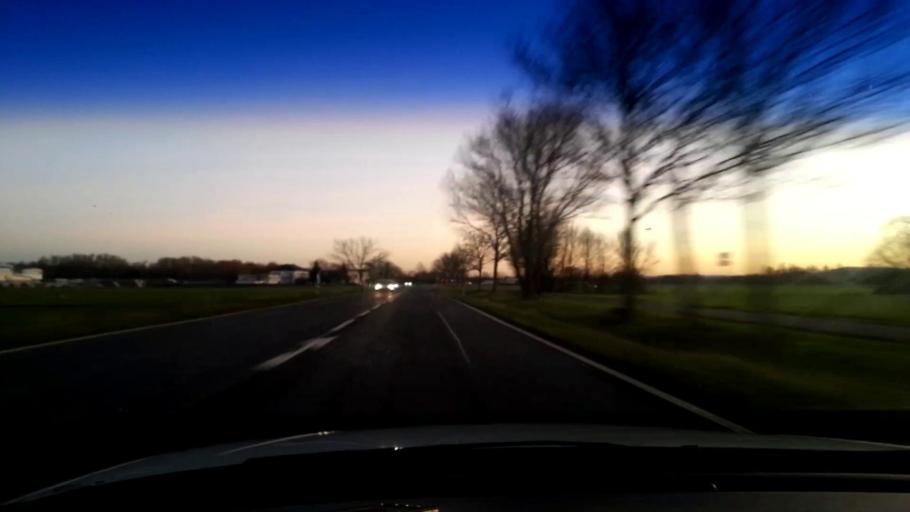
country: DE
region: Bavaria
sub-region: Upper Franconia
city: Breitengussbach
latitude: 49.9911
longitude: 10.8832
